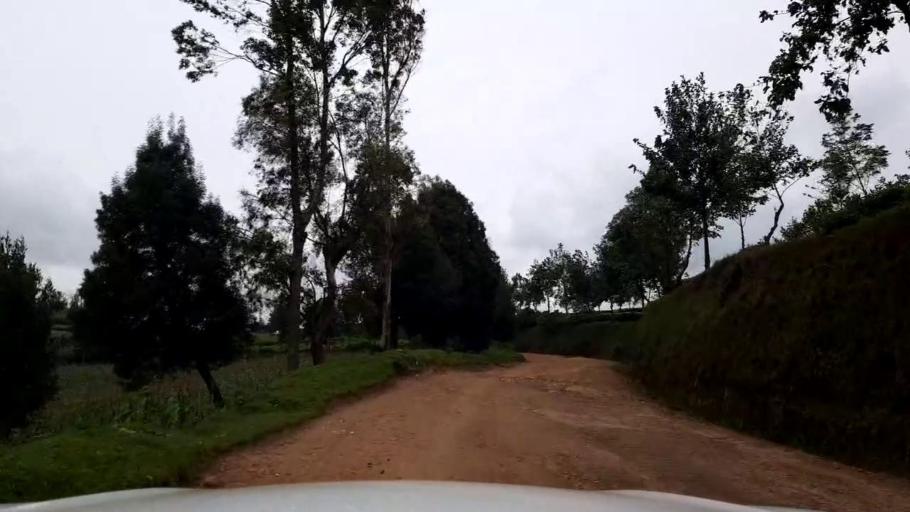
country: RW
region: Western Province
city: Kibuye
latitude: -1.9549
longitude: 29.4036
